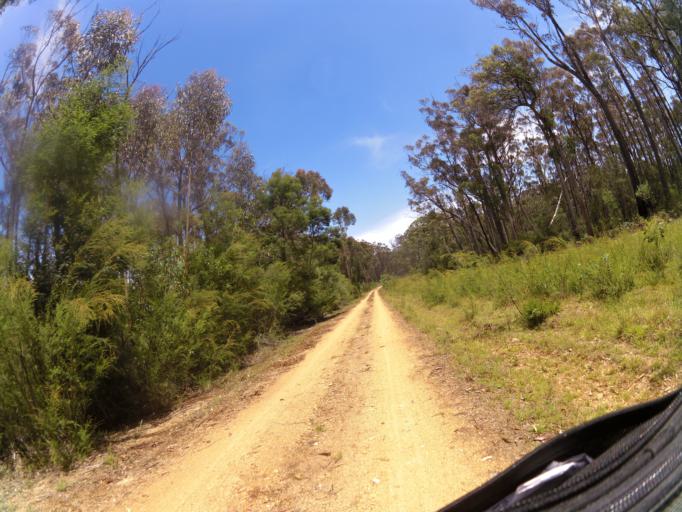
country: AU
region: Victoria
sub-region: East Gippsland
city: Lakes Entrance
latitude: -37.7537
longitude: 147.9710
